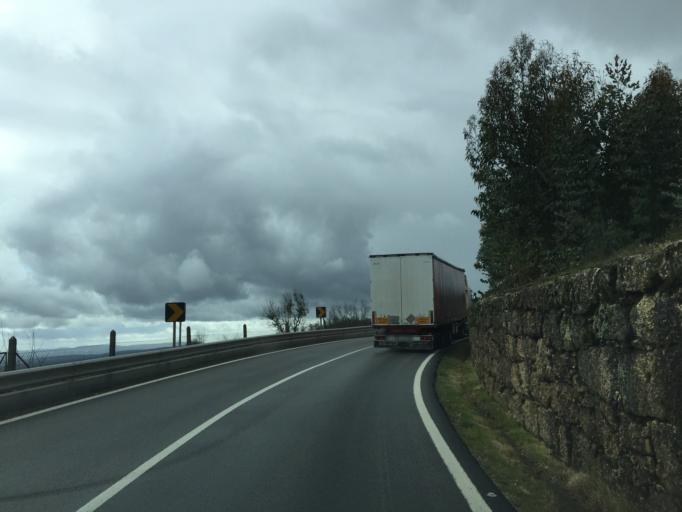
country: PT
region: Coimbra
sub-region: Oliveira do Hospital
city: Oliveira do Hospital
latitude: 40.3223
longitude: -7.9259
